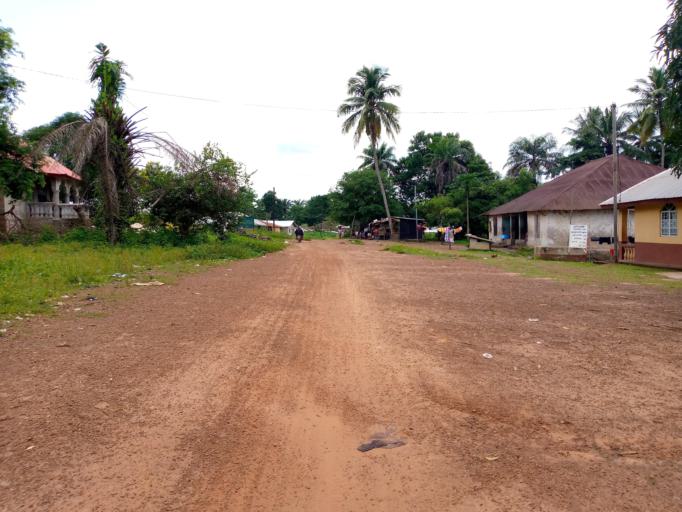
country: SL
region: Northern Province
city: Magburaka
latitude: 8.7104
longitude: -11.9319
